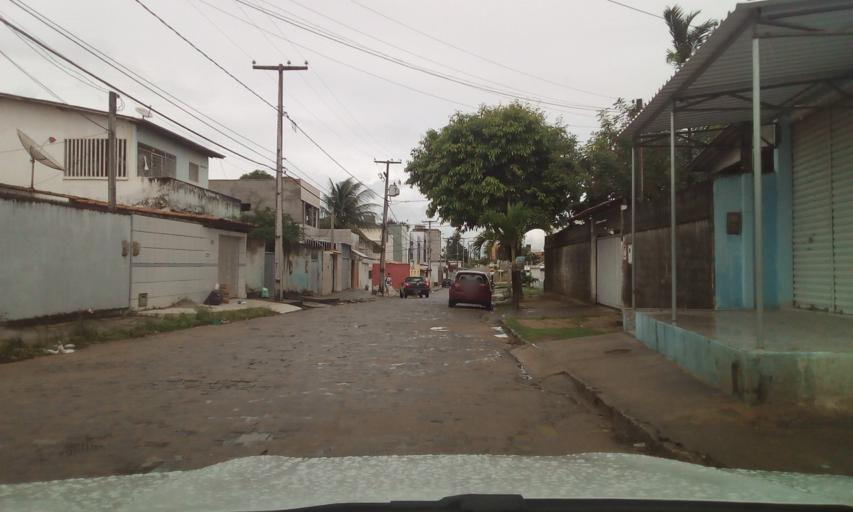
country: BR
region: Paraiba
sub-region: Joao Pessoa
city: Joao Pessoa
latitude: -7.1655
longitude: -34.8484
